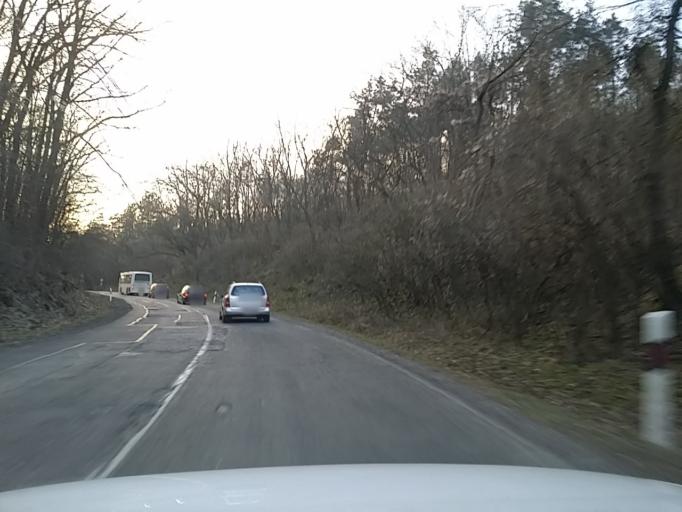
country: HU
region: Nograd
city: Matranovak
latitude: 48.0135
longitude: 20.0284
